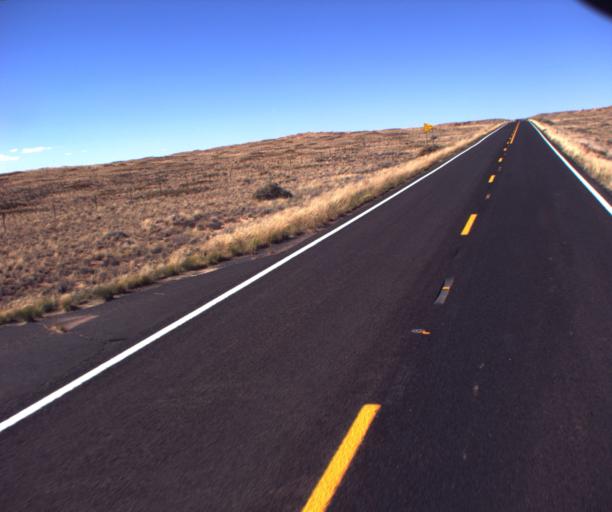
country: US
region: Arizona
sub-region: Coconino County
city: Tuba City
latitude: 35.9532
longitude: -110.9260
